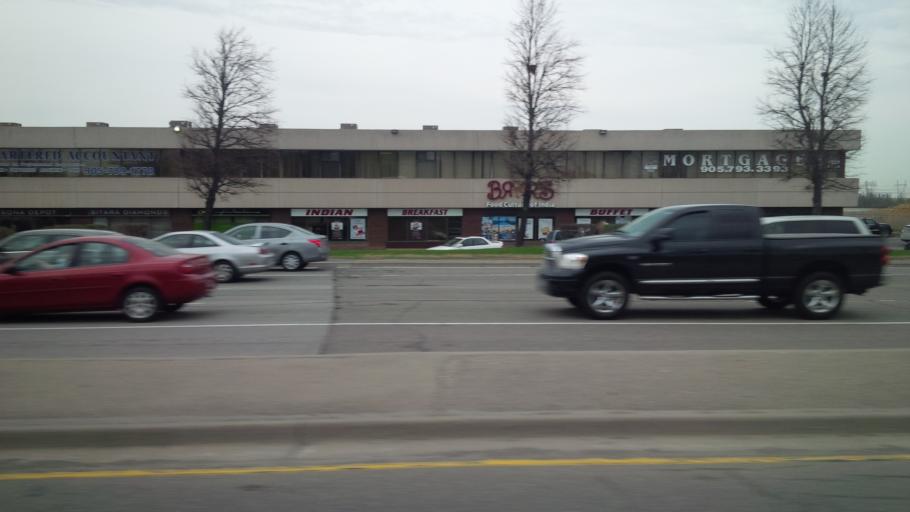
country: CA
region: Ontario
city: Brampton
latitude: 43.6903
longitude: -79.6948
